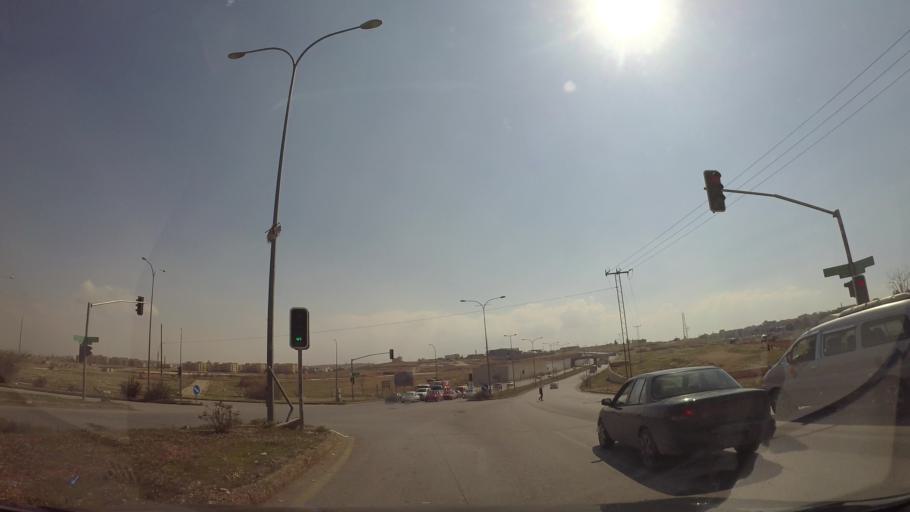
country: JO
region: Zarqa
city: Zarqa
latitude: 32.0738
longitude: 36.1039
